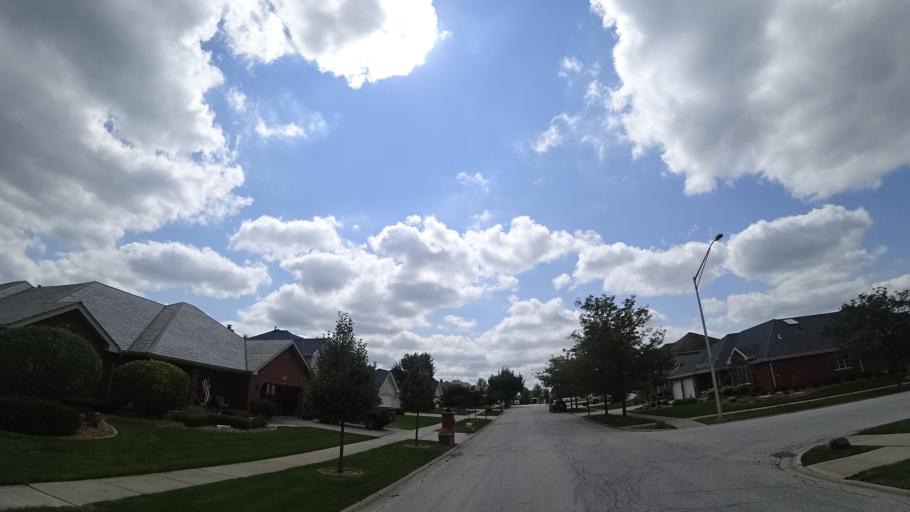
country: US
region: Illinois
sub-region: Cook County
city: Orland Hills
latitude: 41.5710
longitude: -87.8743
